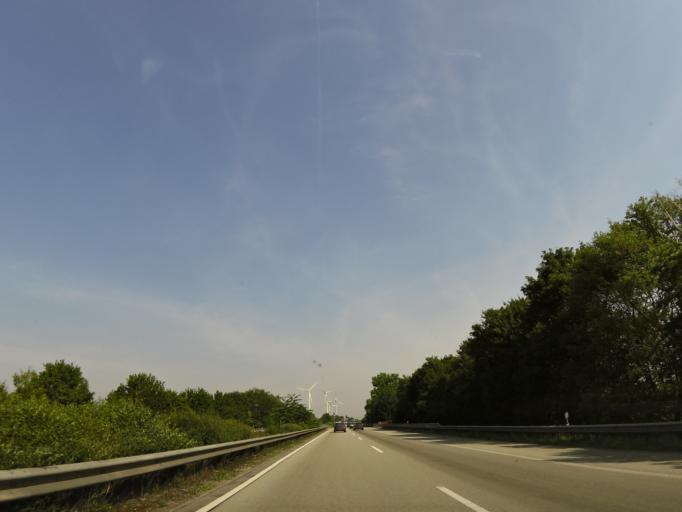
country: DE
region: Rheinland-Pfalz
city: Grossniedesheim
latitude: 49.5698
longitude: 8.3015
